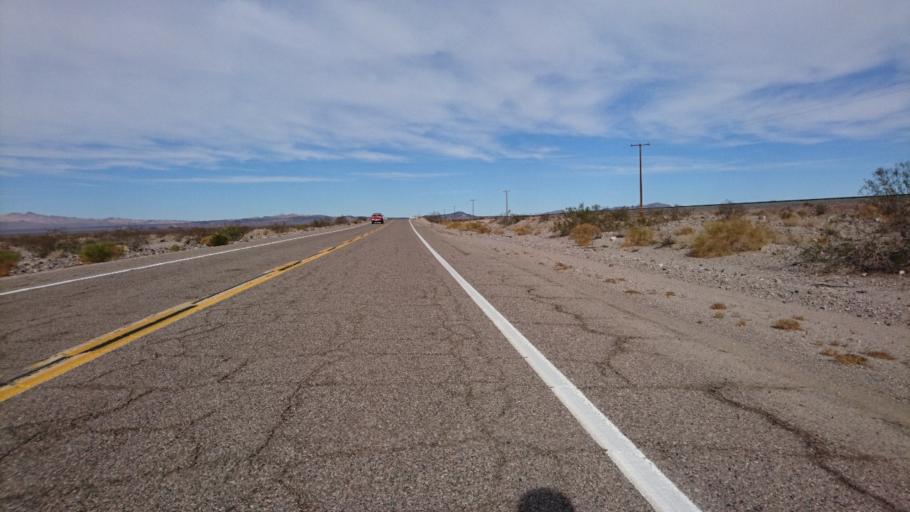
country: US
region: California
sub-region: San Bernardino County
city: Twentynine Palms
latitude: 34.6088
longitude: -115.9671
